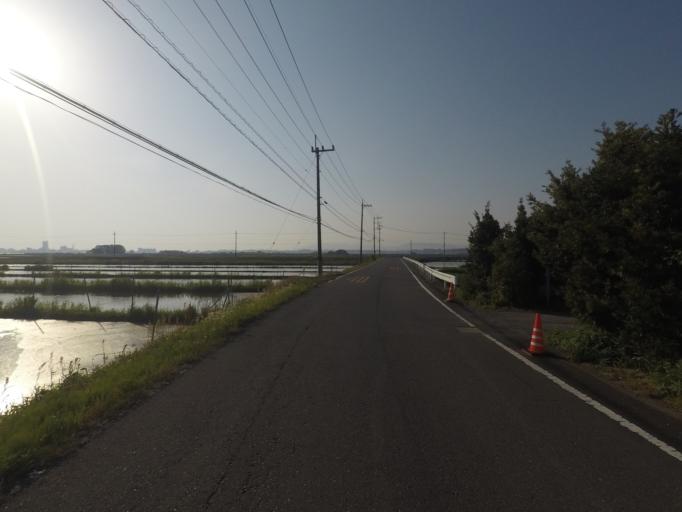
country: JP
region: Ibaraki
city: Ami
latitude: 36.0741
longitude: 140.2466
